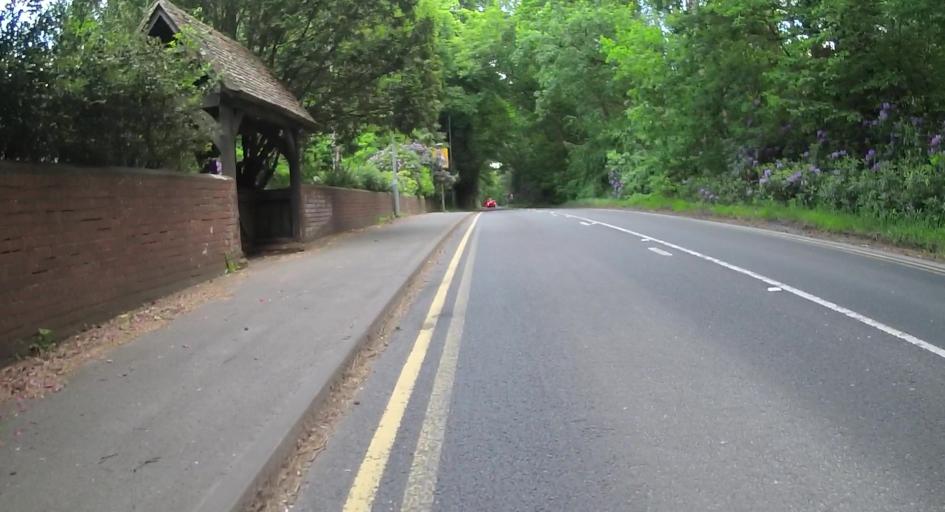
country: GB
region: England
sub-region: Bracknell Forest
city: Crowthorne
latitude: 51.3820
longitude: -0.8167
